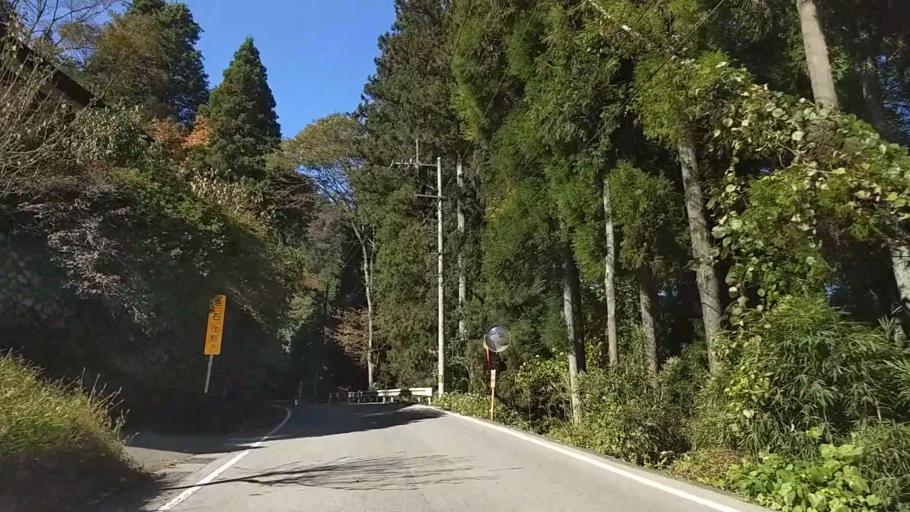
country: JP
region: Yamanashi
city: Uenohara
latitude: 35.6528
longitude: 139.0954
